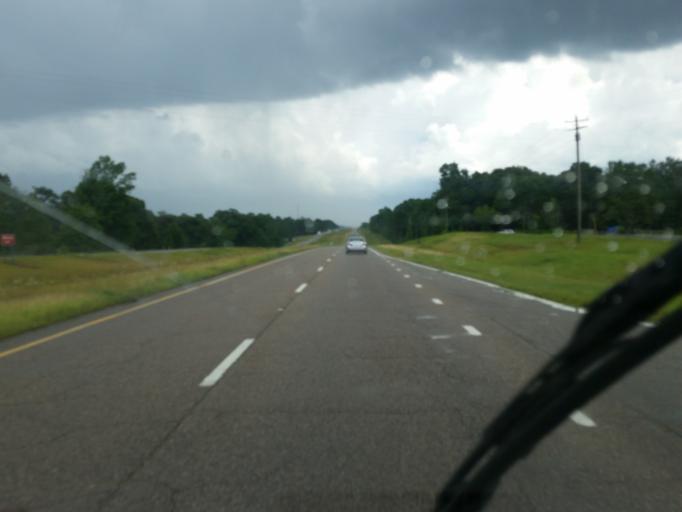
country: US
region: Mississippi
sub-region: George County
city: Lucedale
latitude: 30.9134
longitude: -88.4891
